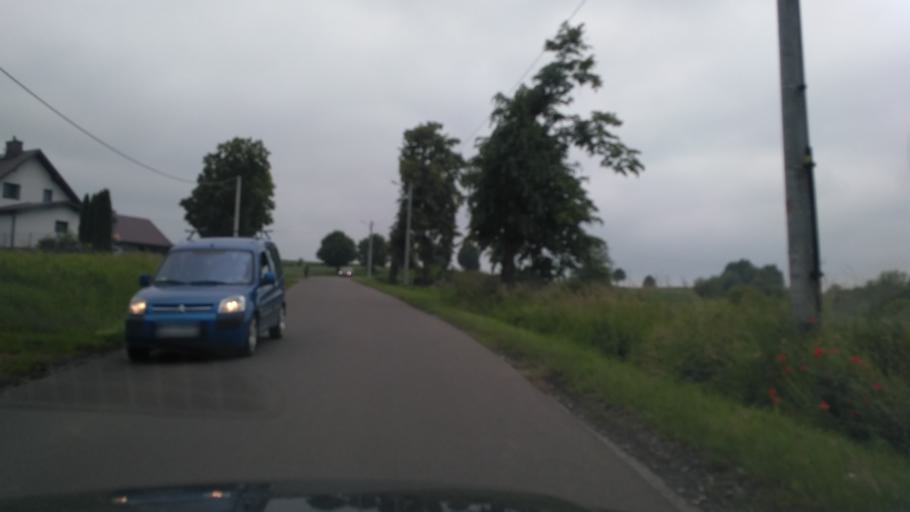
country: PL
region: Subcarpathian Voivodeship
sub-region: Powiat ropczycko-sedziszowski
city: Sedziszow Malopolski
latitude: 50.0482
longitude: 21.6949
